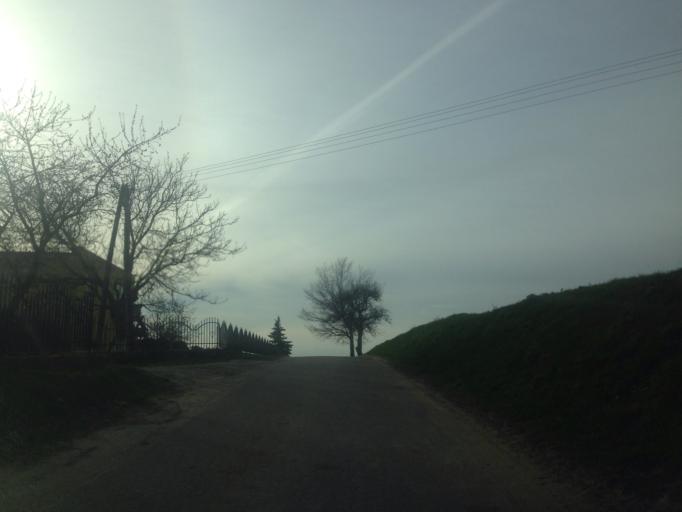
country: PL
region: Kujawsko-Pomorskie
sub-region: Powiat brodnicki
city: Jablonowo Pomorskie
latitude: 53.4229
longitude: 19.2053
